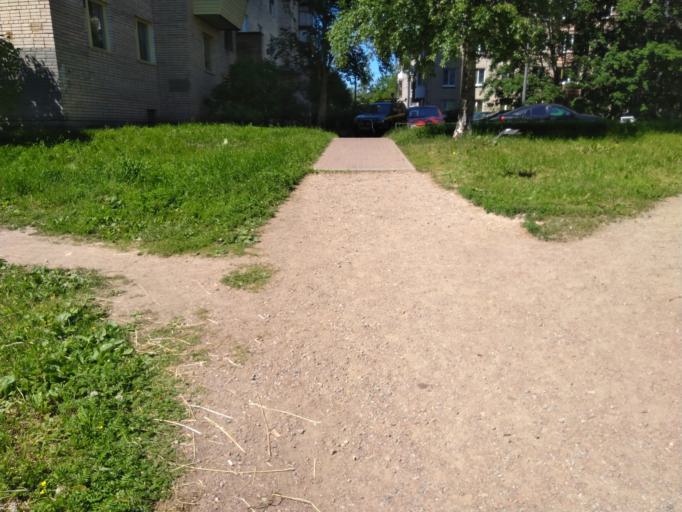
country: RU
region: St.-Petersburg
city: Strel'na
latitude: 59.8516
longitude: 30.0255
